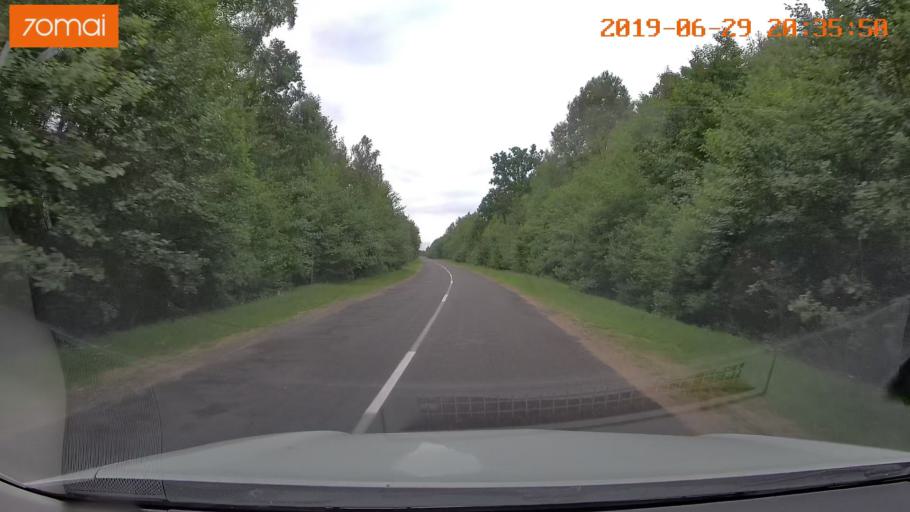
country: BY
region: Brest
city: Hantsavichy
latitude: 52.5198
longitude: 26.3538
